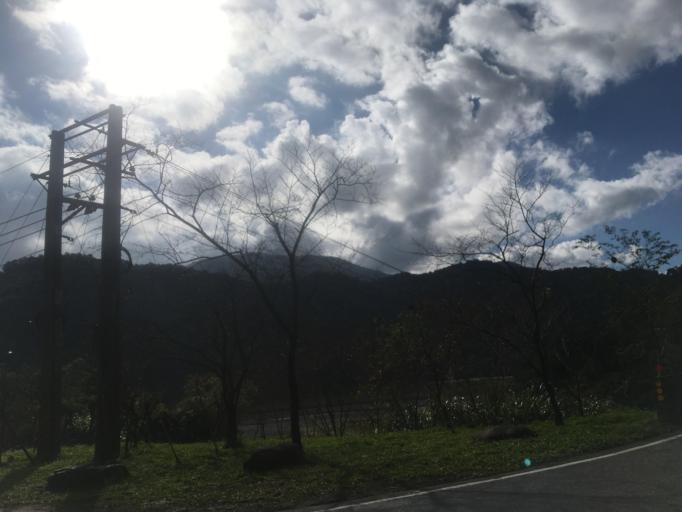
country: TW
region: Taiwan
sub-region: Yilan
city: Yilan
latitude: 24.6391
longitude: 121.5536
